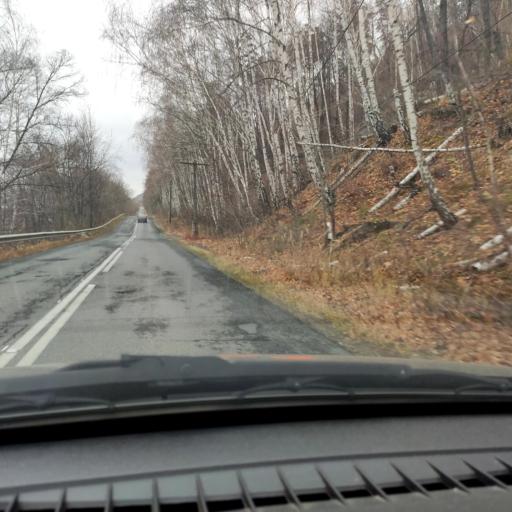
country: RU
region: Samara
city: Pribrezhnyy
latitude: 53.4421
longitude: 49.7772
